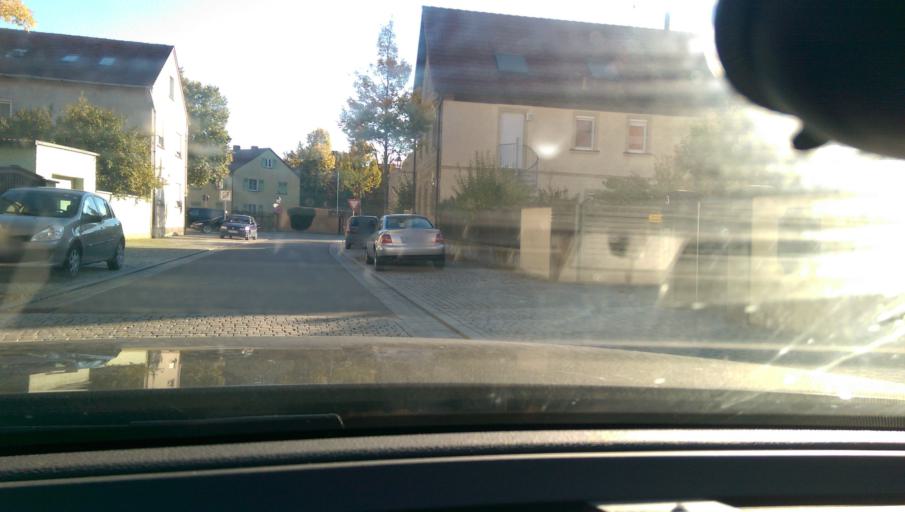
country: DE
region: Bavaria
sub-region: Regierungsbezirk Unterfranken
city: Grafenrheinfeld
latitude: 50.0041
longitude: 10.1977
